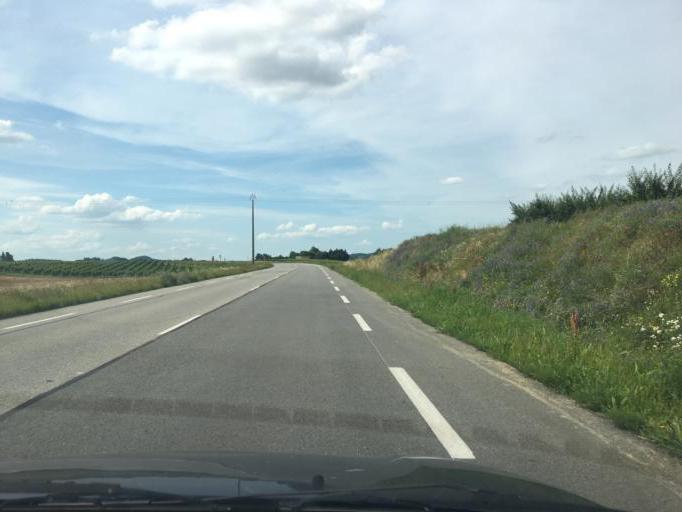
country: FR
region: Rhone-Alpes
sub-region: Departement de la Drome
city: Clerieux
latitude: 45.0842
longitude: 4.9372
